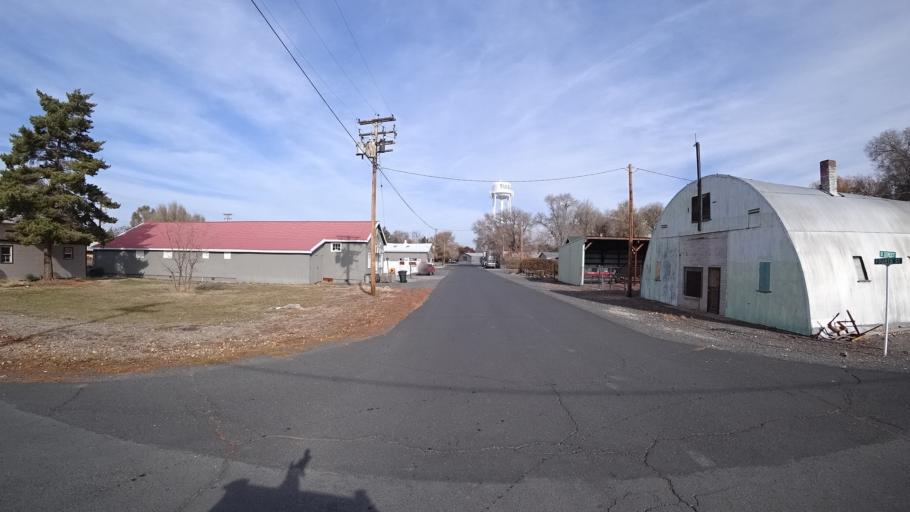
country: US
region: California
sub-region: Siskiyou County
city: Tulelake
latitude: 41.9549
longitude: -121.4753
